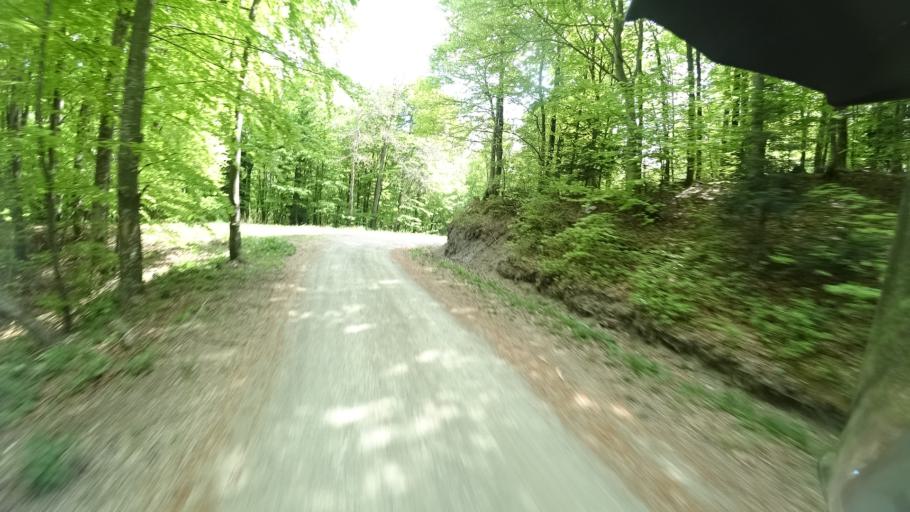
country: HR
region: Grad Zagreb
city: Kasina
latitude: 45.9000
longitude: 15.9887
